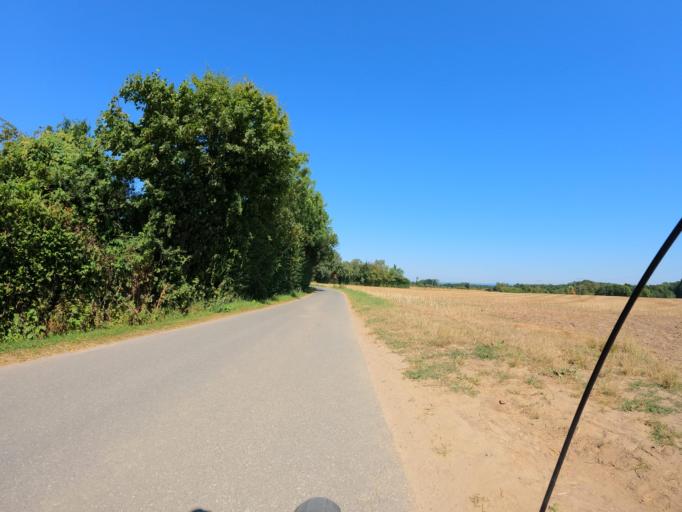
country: DE
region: Schleswig-Holstein
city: Steinberg
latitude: 54.7819
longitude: 9.7609
